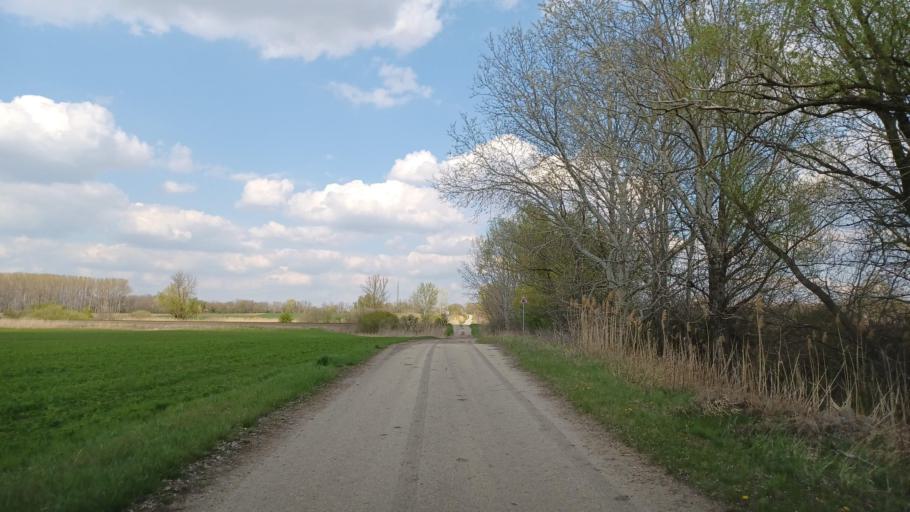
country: HU
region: Fejer
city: Cece
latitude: 46.7407
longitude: 18.6401
